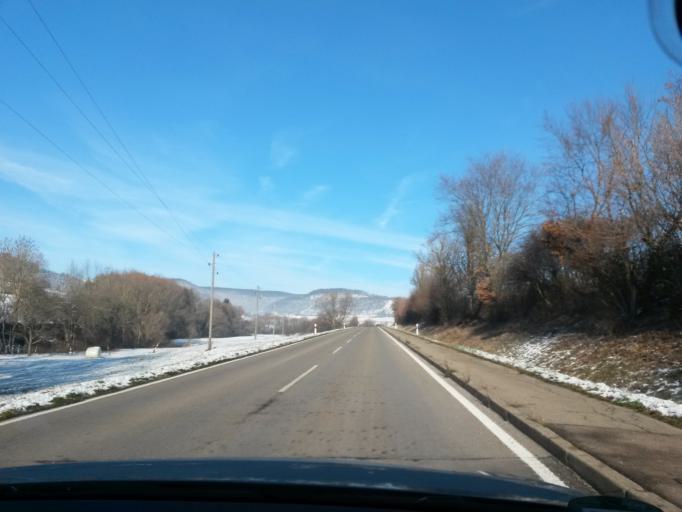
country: DE
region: Baden-Wuerttemberg
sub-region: Regierungsbezirk Stuttgart
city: Bad Uberkingen
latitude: 48.6121
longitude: 9.7614
